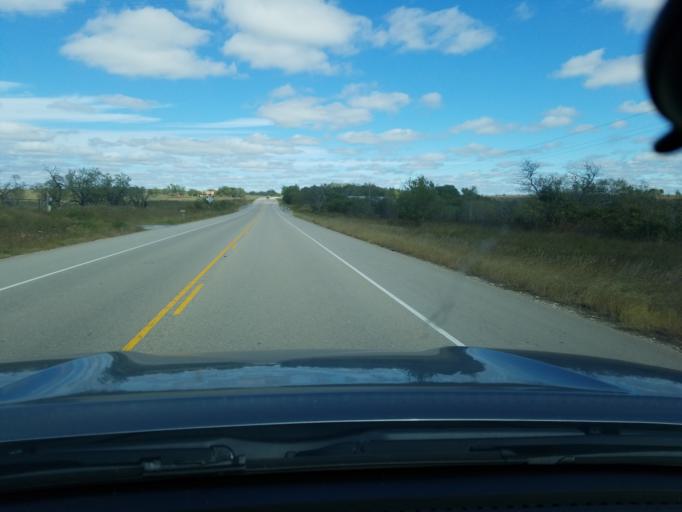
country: US
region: Texas
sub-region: Hamilton County
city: Hamilton
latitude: 31.6418
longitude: -98.1492
